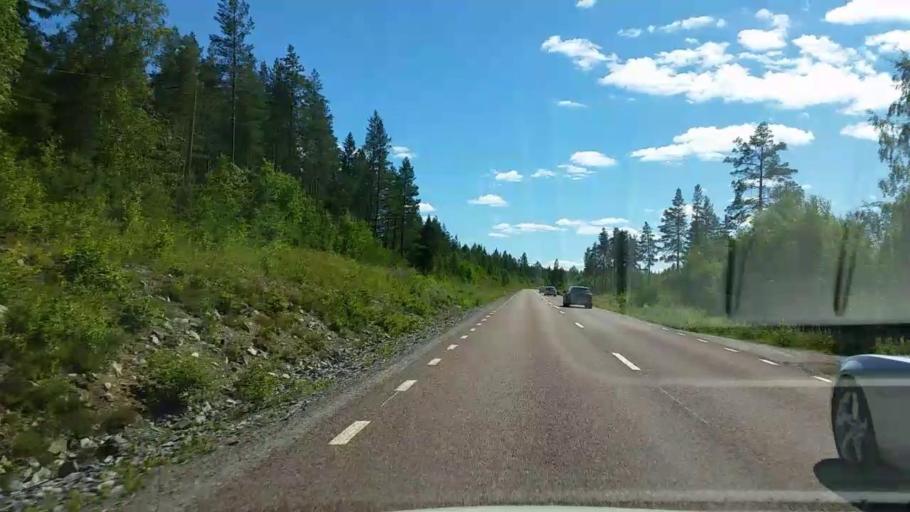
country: SE
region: Gaevleborg
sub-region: Ovanakers Kommun
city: Edsbyn
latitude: 61.2208
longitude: 15.8769
